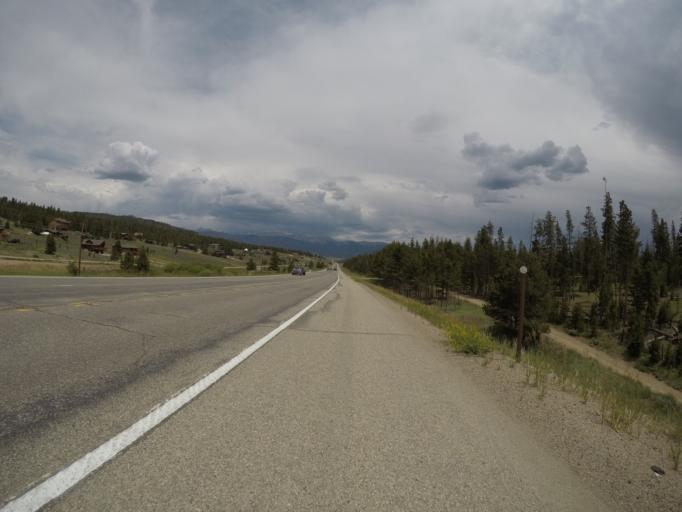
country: US
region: Colorado
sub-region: Grand County
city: Fraser
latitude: 39.9976
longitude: -105.8952
